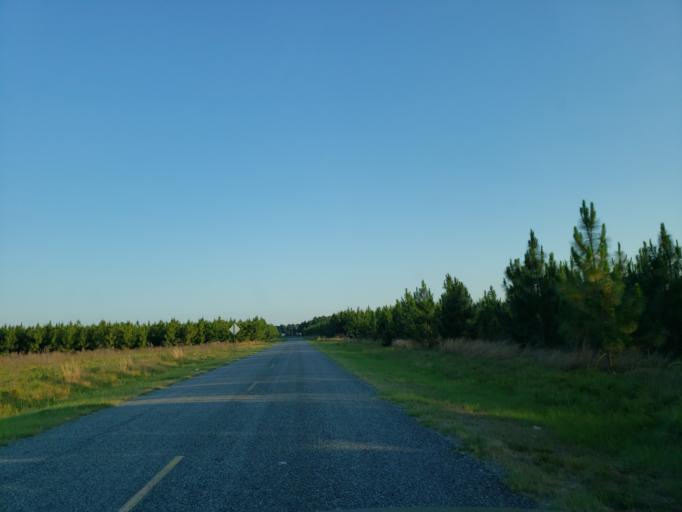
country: US
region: Georgia
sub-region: Dooly County
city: Vienna
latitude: 32.1118
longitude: -83.7558
